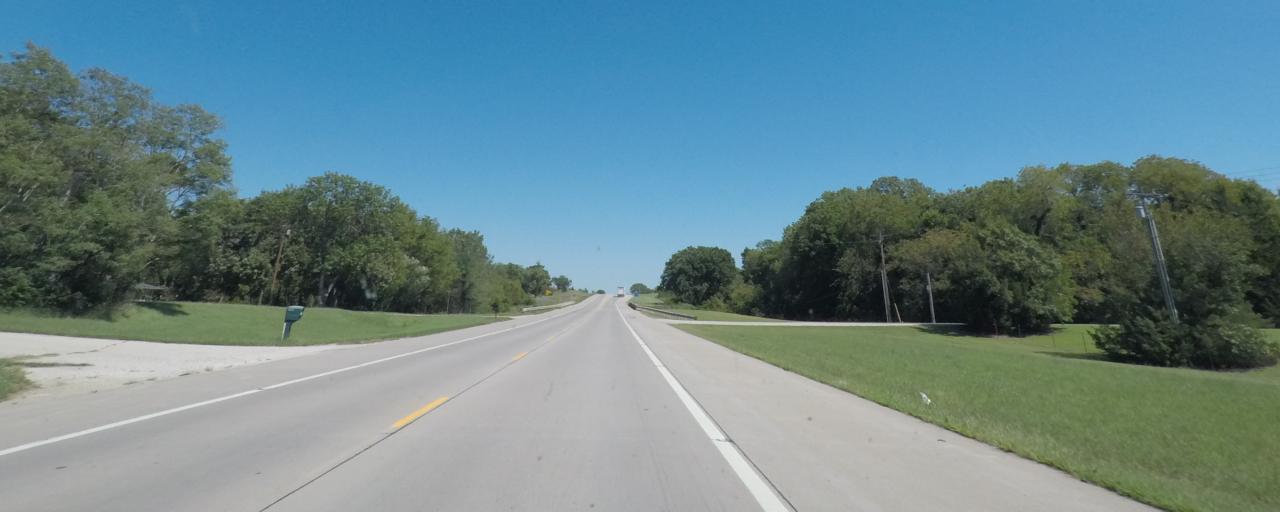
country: US
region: Kansas
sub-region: Lyon County
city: Emporia
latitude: 38.4124
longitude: -96.2682
